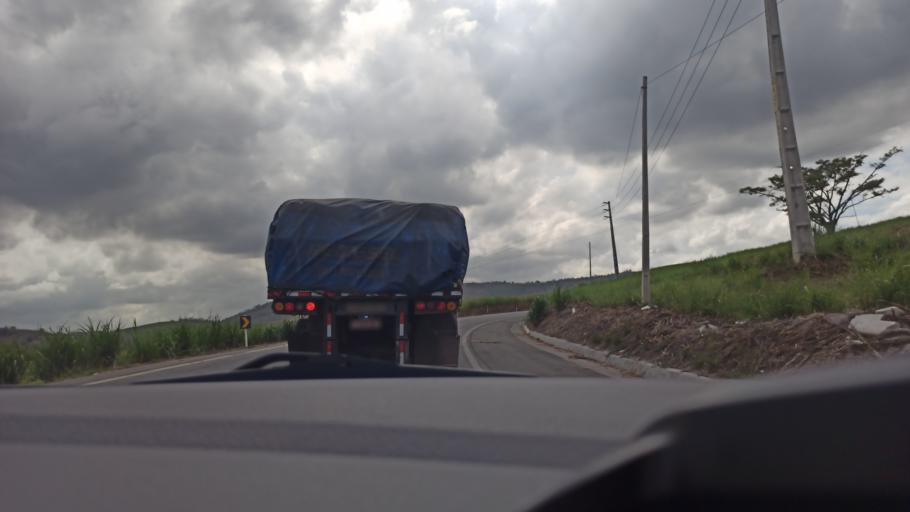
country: BR
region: Pernambuco
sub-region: Timbauba
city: Timbauba
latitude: -7.5228
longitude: -35.2936
